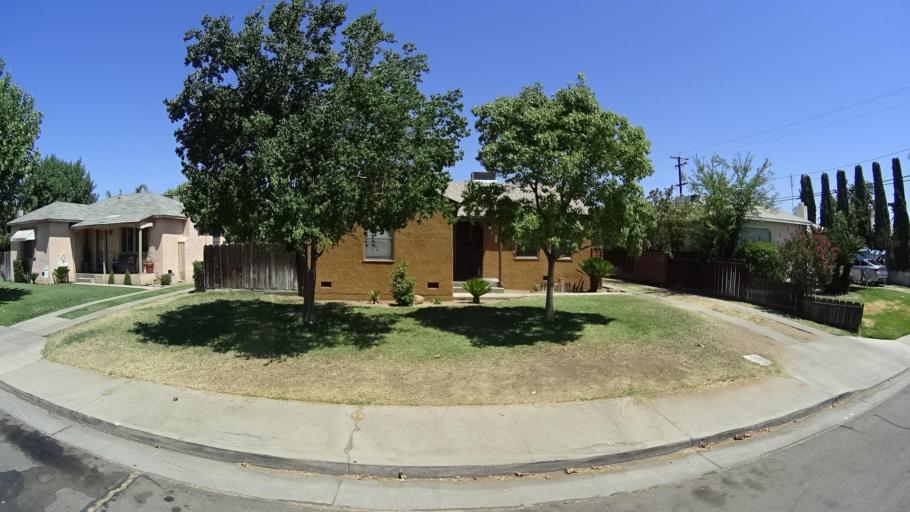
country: US
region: California
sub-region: Fresno County
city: Fresno
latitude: 36.7401
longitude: -119.7403
